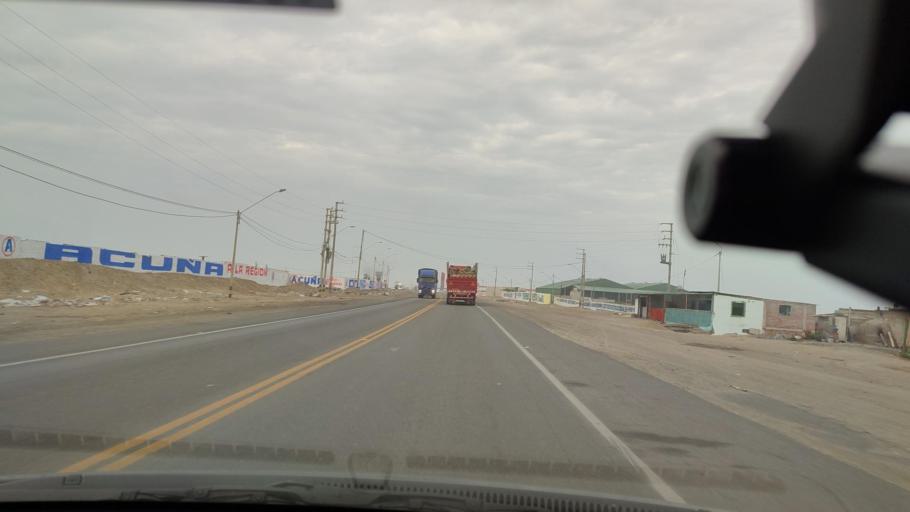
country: PE
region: La Libertad
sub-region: Provincia de Trujillo
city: Huanchaco
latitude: -8.0980
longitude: -79.0991
